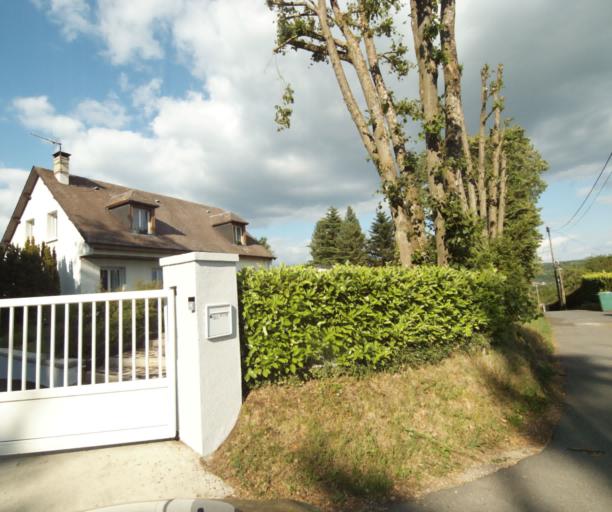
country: FR
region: Champagne-Ardenne
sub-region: Departement des Ardennes
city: Charleville-Mezieres
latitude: 49.7768
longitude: 4.7268
